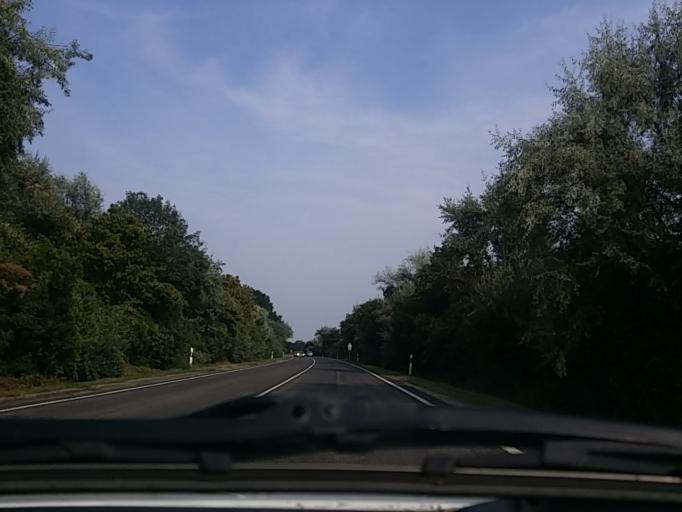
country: HU
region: Fejer
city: Szarliget
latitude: 47.4834
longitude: 18.5370
